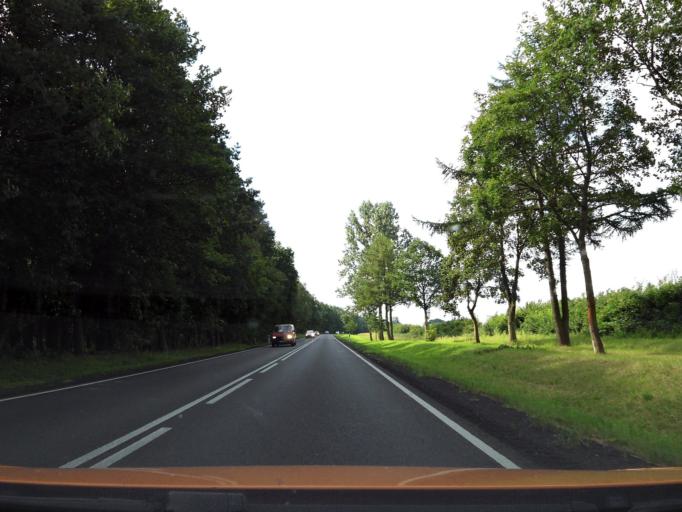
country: PL
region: West Pomeranian Voivodeship
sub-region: Powiat gryficki
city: Ploty
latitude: 53.8452
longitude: 15.3136
